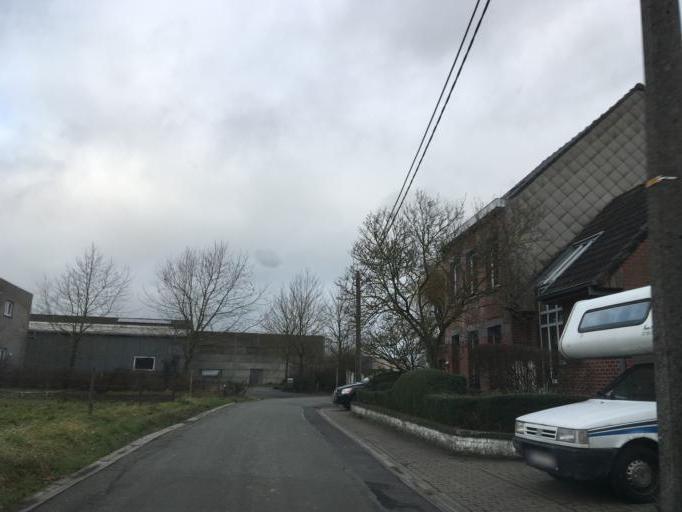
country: BE
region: Flanders
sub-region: Provincie West-Vlaanderen
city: Roeselare
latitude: 50.9747
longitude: 3.1131
